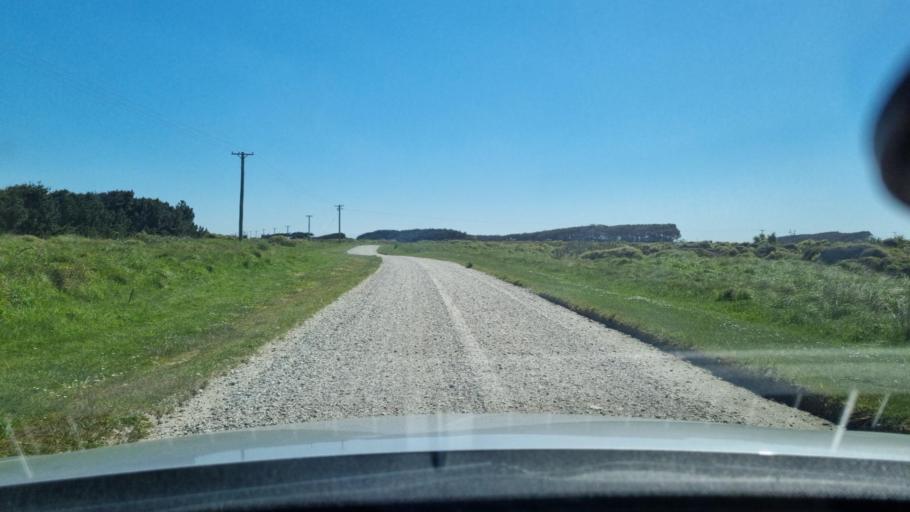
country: NZ
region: Southland
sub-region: Invercargill City
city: Invercargill
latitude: -46.4366
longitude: 168.2382
